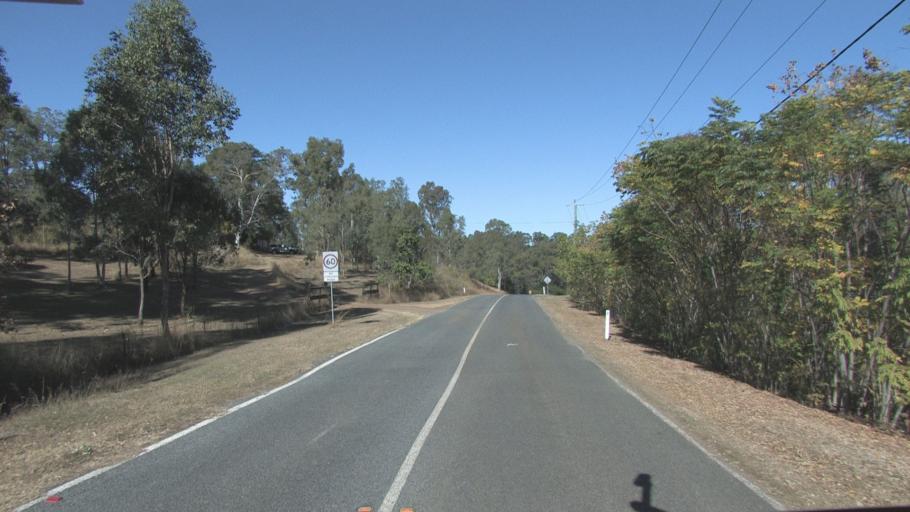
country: AU
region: Queensland
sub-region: Logan
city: Cedar Vale
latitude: -27.8865
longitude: 152.9952
